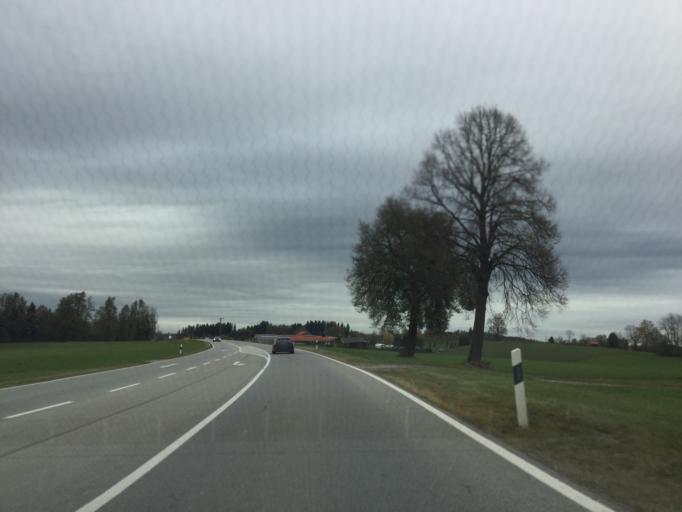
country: DE
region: Bavaria
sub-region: Upper Bavaria
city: Murnau am Staffelsee
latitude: 47.6962
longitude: 11.2042
